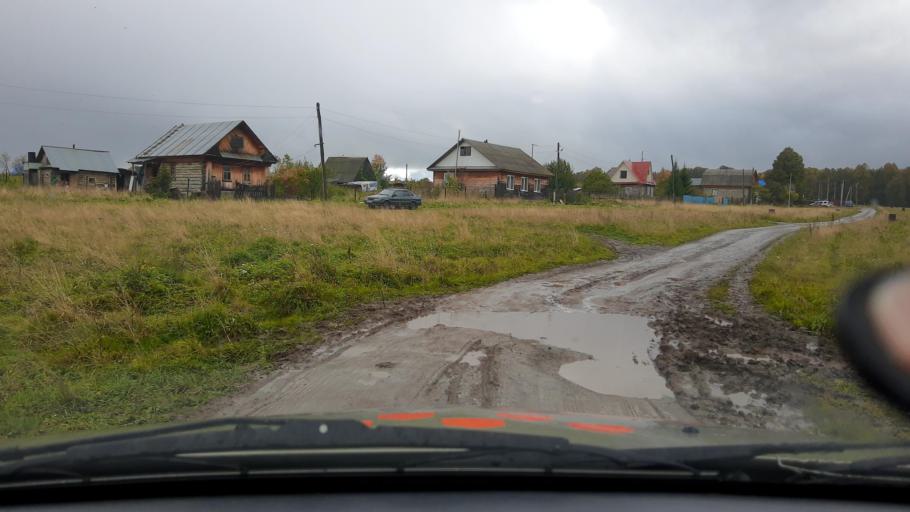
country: RU
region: Bashkortostan
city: Kudeyevskiy
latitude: 54.8766
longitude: 56.6289
